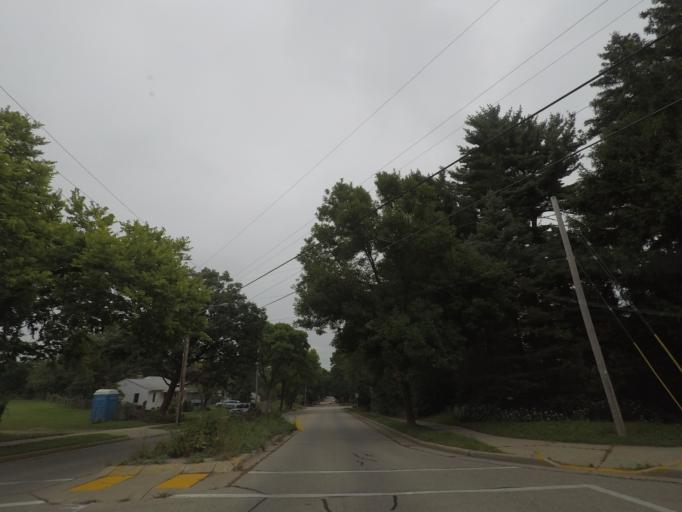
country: US
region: Wisconsin
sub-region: Dane County
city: Shorewood Hills
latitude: 43.0401
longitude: -89.4488
